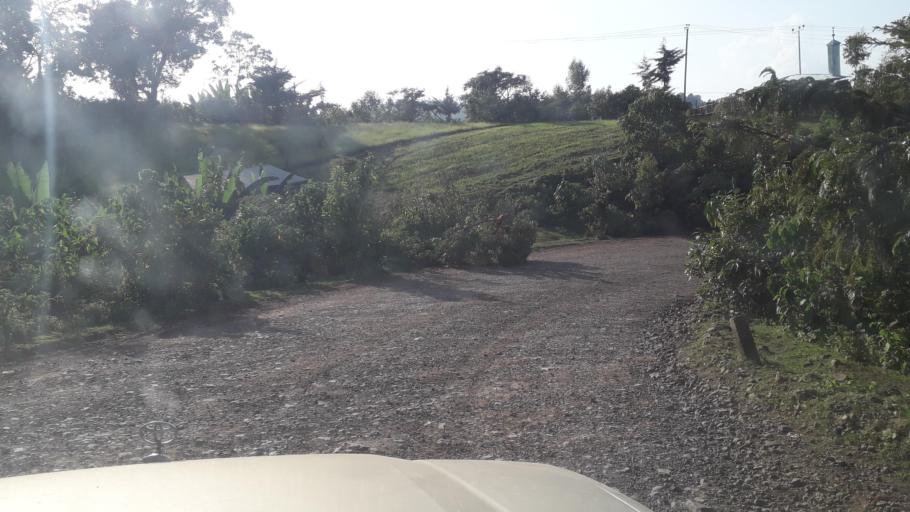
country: ET
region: Oromiya
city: Jima
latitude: 7.4721
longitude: 36.8776
